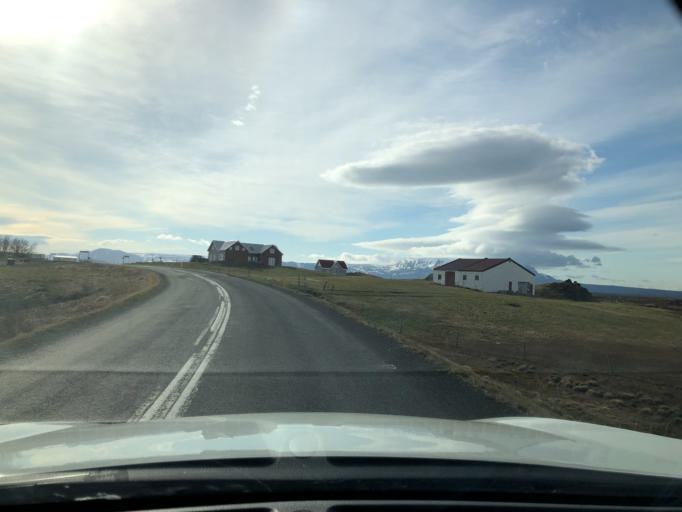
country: IS
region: Northeast
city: Laugar
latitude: 65.5700
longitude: -17.0504
